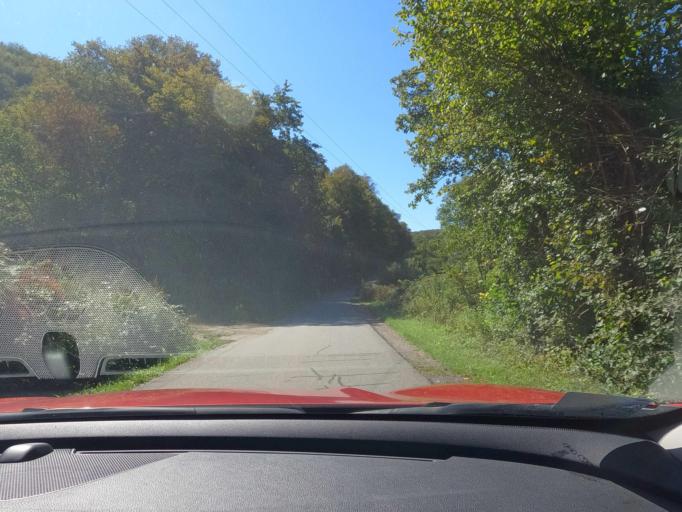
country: HR
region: Sisacko-Moslavacka
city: Petrinja
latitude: 45.4022
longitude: 16.2464
